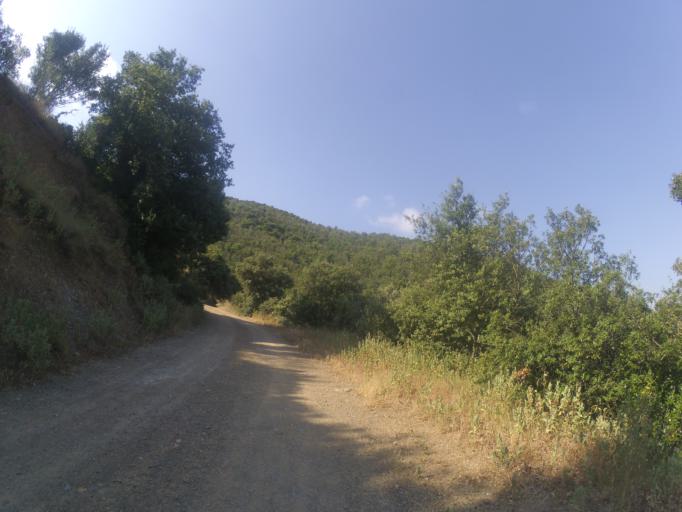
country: FR
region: Languedoc-Roussillon
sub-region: Departement des Pyrenees-Orientales
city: Ille-sur-Tet
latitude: 42.6481
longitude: 2.6404
